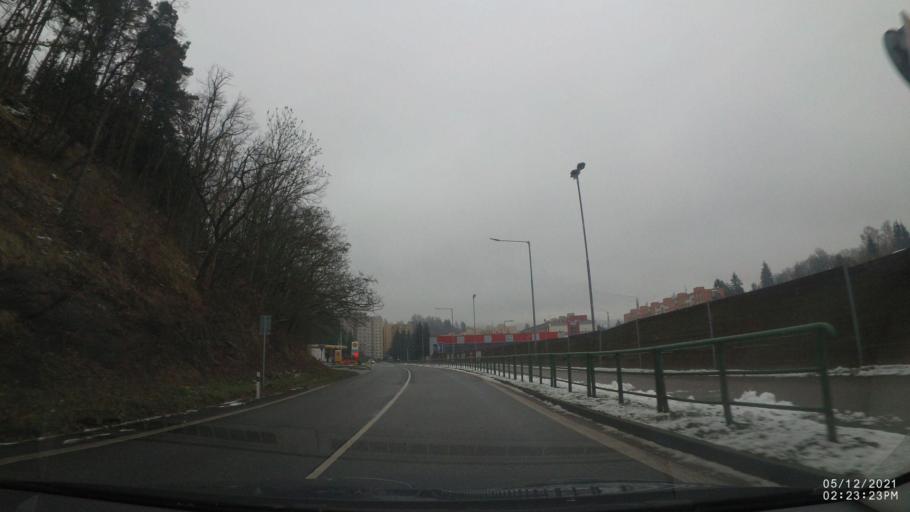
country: CZ
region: Kralovehradecky
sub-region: Okres Nachod
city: Nachod
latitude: 50.4252
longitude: 16.1601
